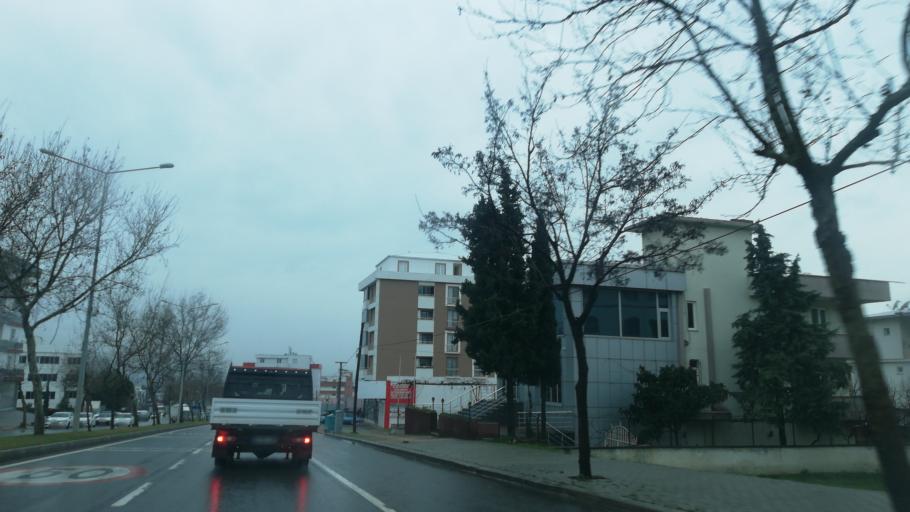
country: TR
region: Kahramanmaras
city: Kahramanmaras
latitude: 37.5690
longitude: 36.9425
